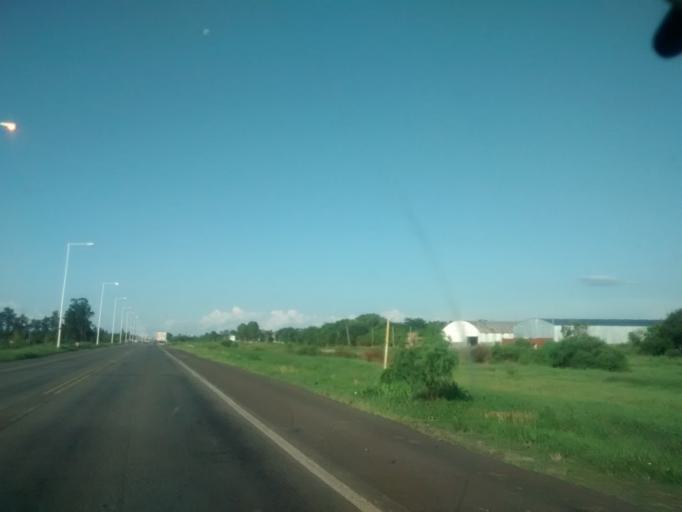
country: AR
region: Chaco
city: Fontana
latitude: -27.4648
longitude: -59.0444
